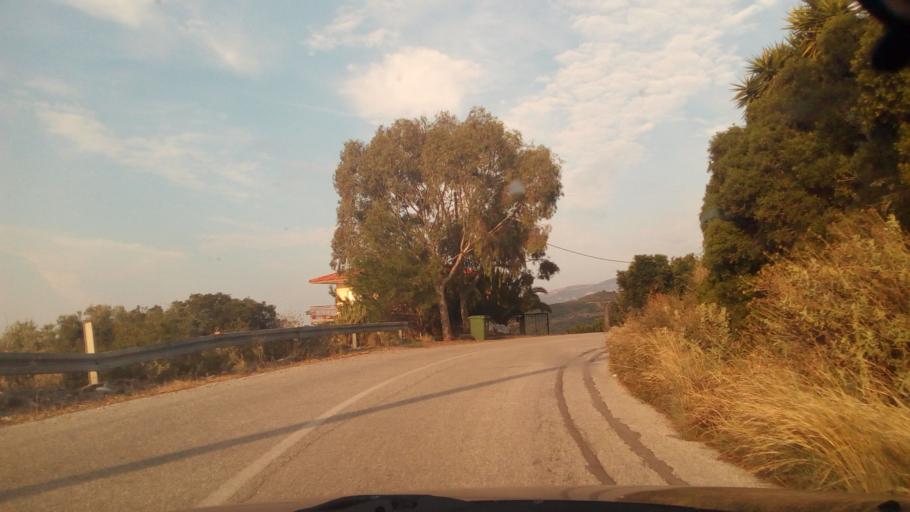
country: GR
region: West Greece
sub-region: Nomos Aitolias kai Akarnanias
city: Nafpaktos
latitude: 38.4085
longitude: 21.9339
